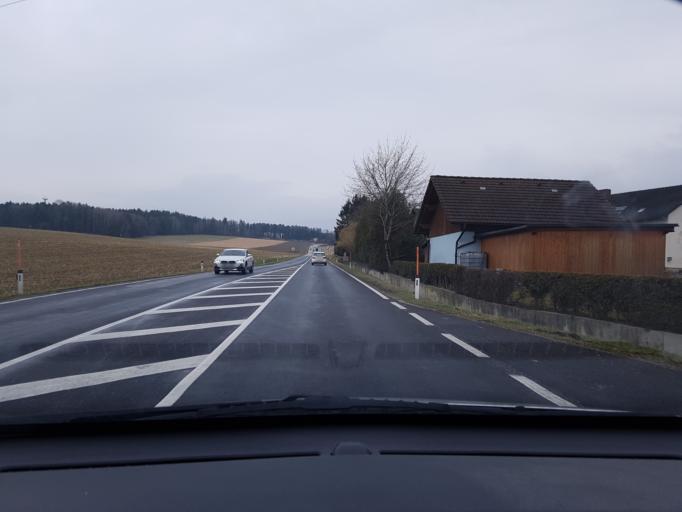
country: AT
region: Upper Austria
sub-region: Steyr Stadt
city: Steyr
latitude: 48.0697
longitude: 14.3836
